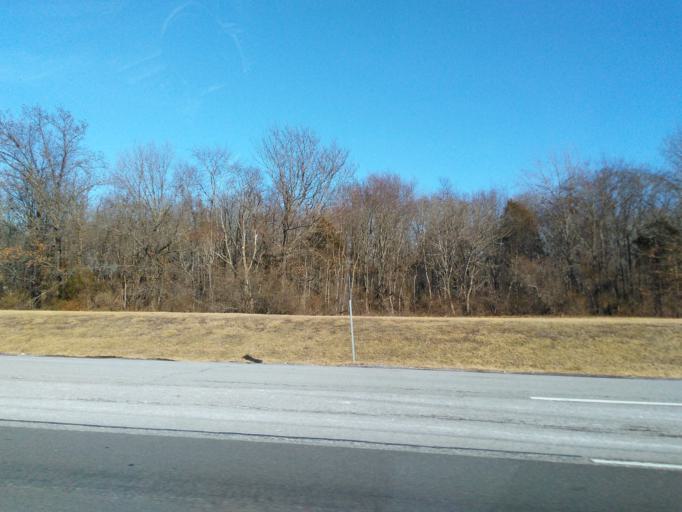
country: US
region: Illinois
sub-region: Franklin County
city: Benton
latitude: 38.0331
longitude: -88.9252
